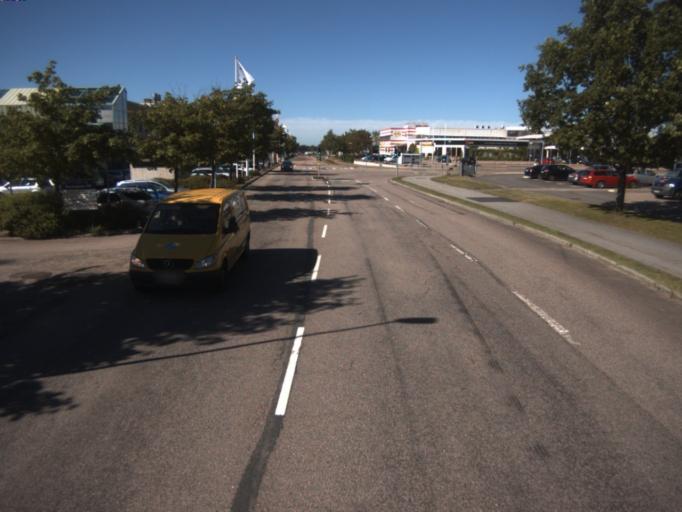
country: SE
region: Skane
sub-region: Helsingborg
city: Odakra
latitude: 56.0896
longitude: 12.7451
